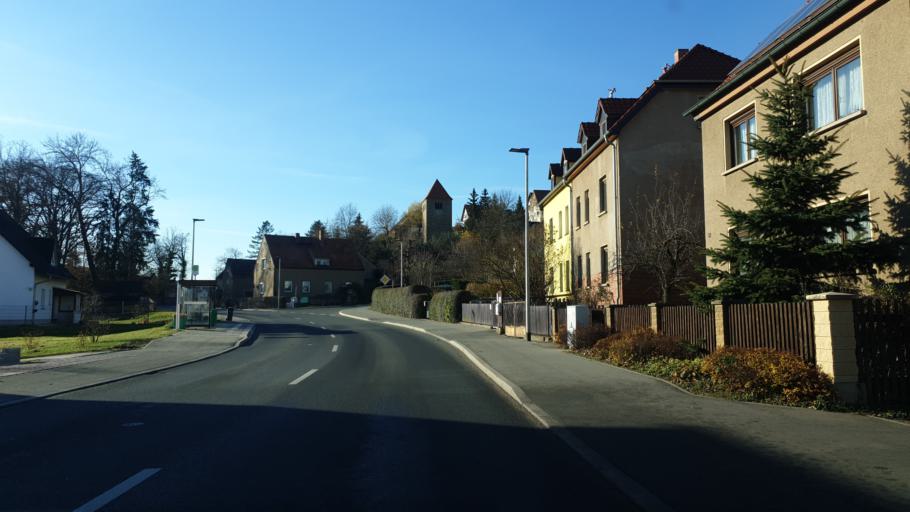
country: DE
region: Thuringia
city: Hartmannsdorf
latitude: 50.9624
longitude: 11.9789
